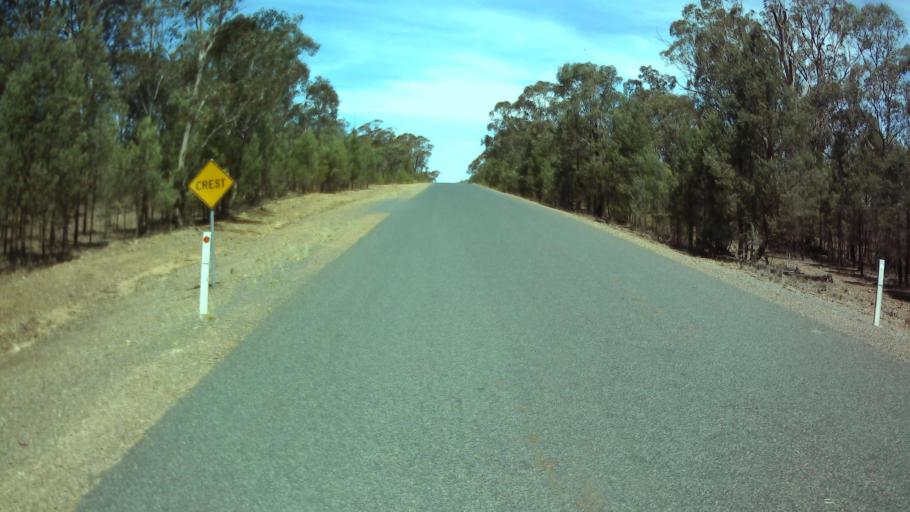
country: AU
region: New South Wales
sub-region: Weddin
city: Grenfell
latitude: -33.9002
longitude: 147.7549
